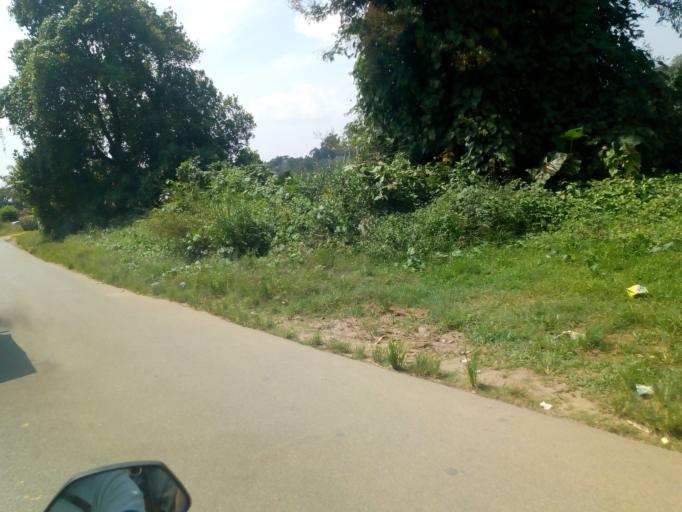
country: IN
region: Karnataka
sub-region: Kodagu
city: Ponnampet
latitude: 12.0847
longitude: 75.9426
